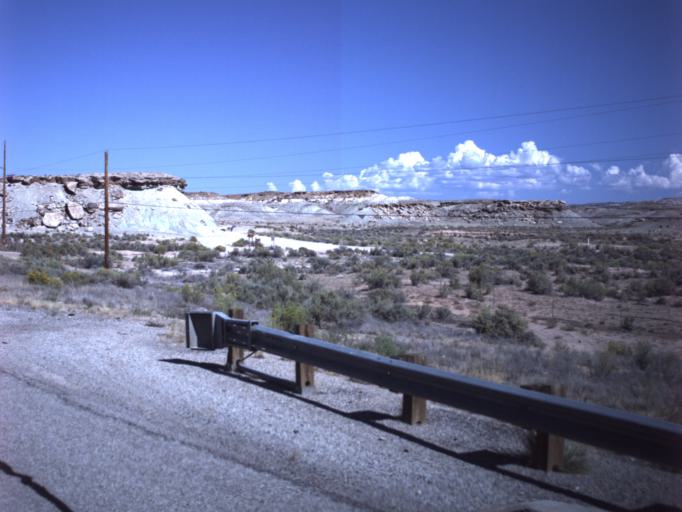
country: US
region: Utah
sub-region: Grand County
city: Moab
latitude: 38.7287
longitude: -109.7240
